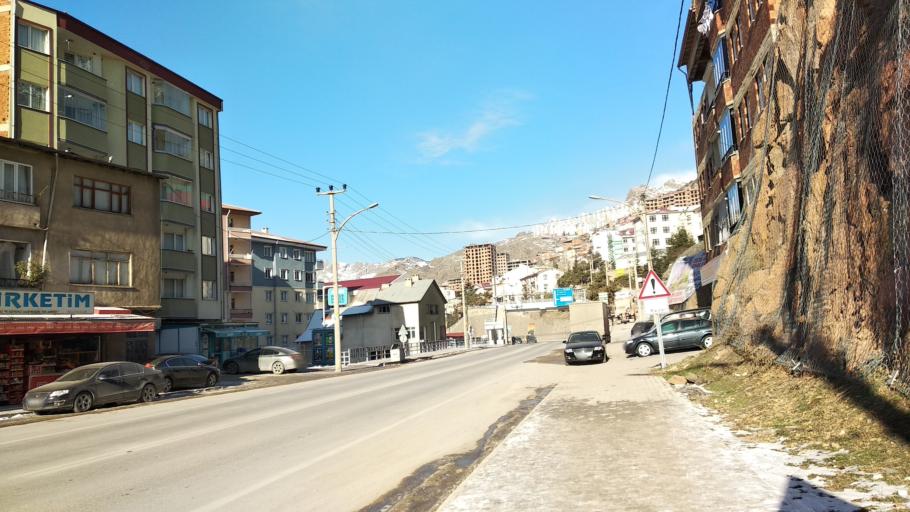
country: TR
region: Gumushane
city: Gumushkhane
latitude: 40.4561
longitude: 39.4902
